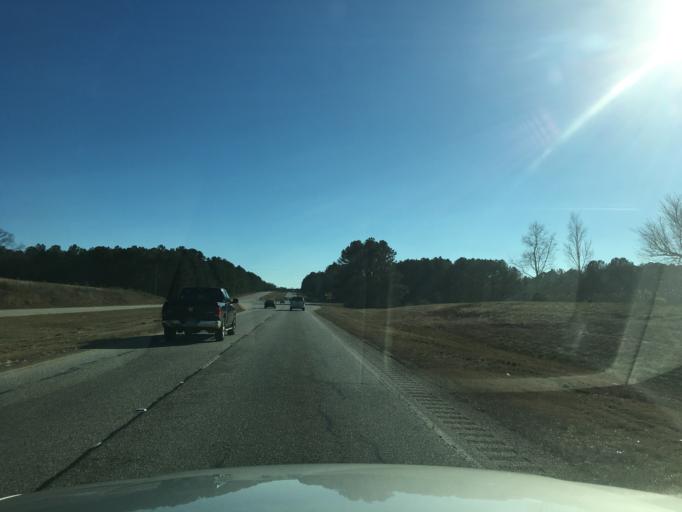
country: US
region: Georgia
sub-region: Carroll County
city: Carrollton
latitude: 33.5855
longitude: -85.0418
